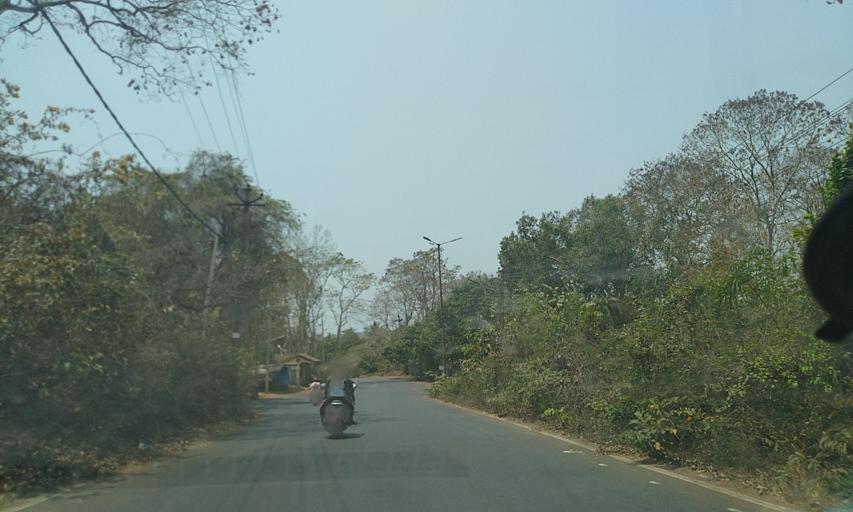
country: IN
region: Goa
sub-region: North Goa
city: Mapuca
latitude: 15.5968
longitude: 73.7923
